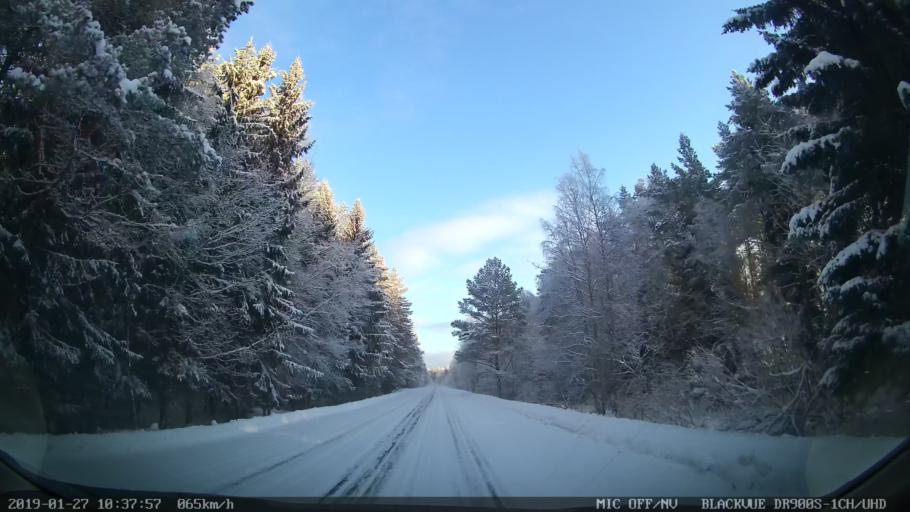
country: EE
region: Harju
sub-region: Raasiku vald
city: Raasiku
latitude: 59.4773
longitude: 25.2518
